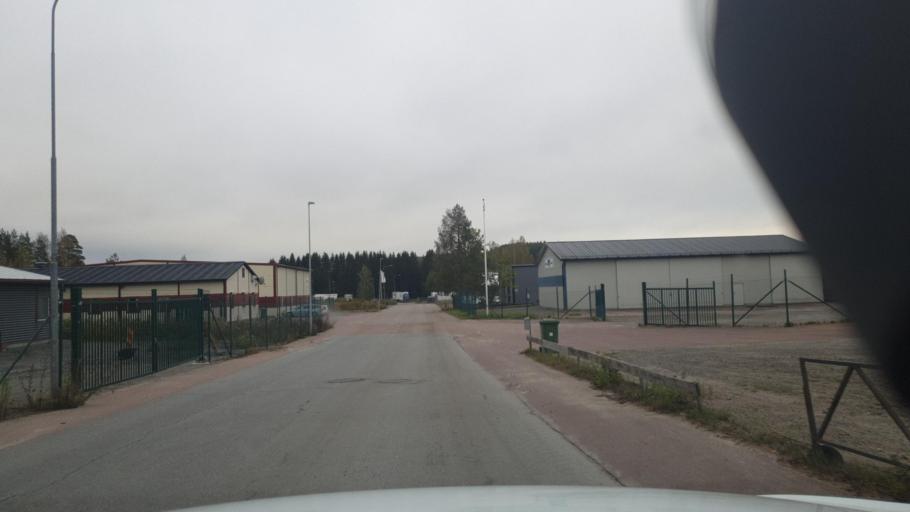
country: SE
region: Vaermland
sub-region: Arvika Kommun
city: Arvika
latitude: 59.6660
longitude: 12.6310
